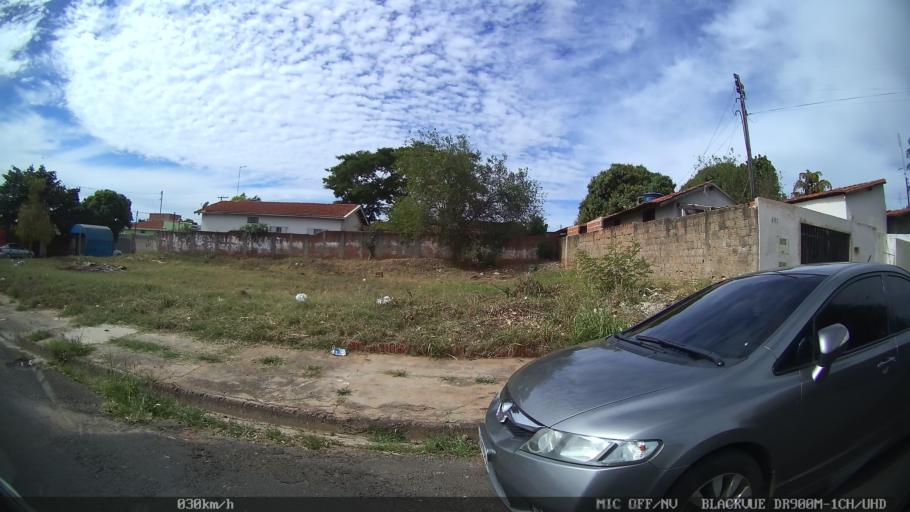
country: BR
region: Sao Paulo
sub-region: Catanduva
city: Catanduva
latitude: -21.1494
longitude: -48.9686
